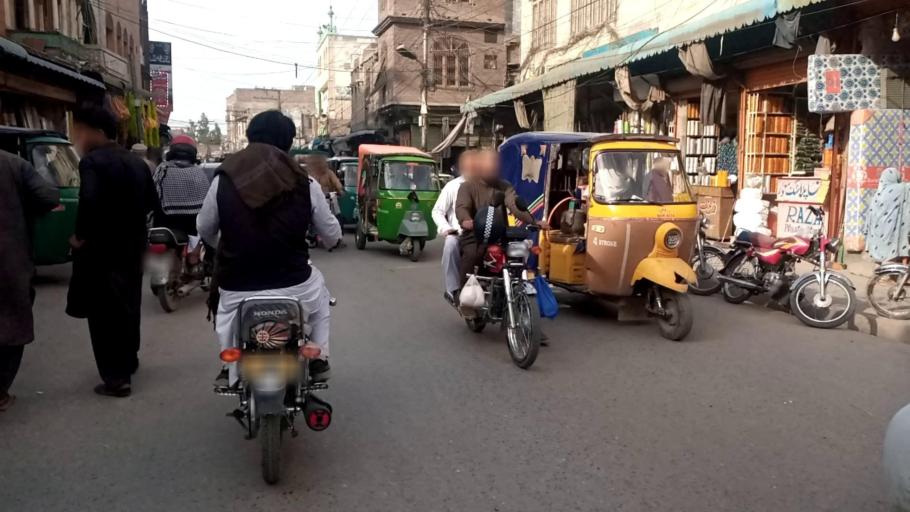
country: PK
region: Khyber Pakhtunkhwa
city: Peshawar
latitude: 34.0116
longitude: 71.5746
